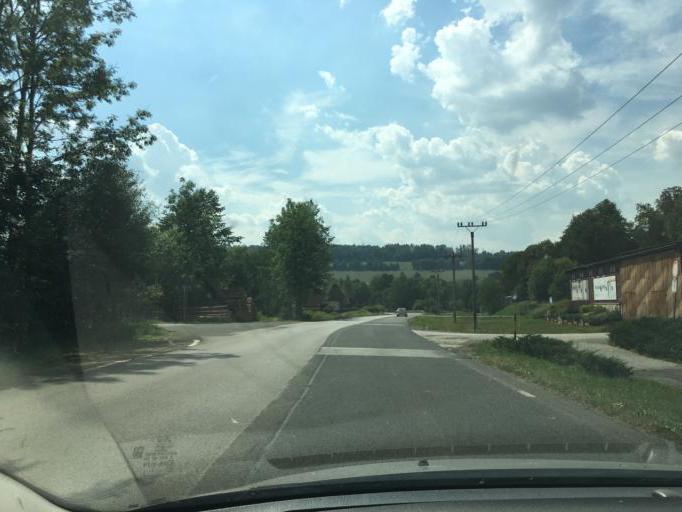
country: CZ
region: Liberecky
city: Jilemnice
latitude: 50.6254
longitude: 15.5121
